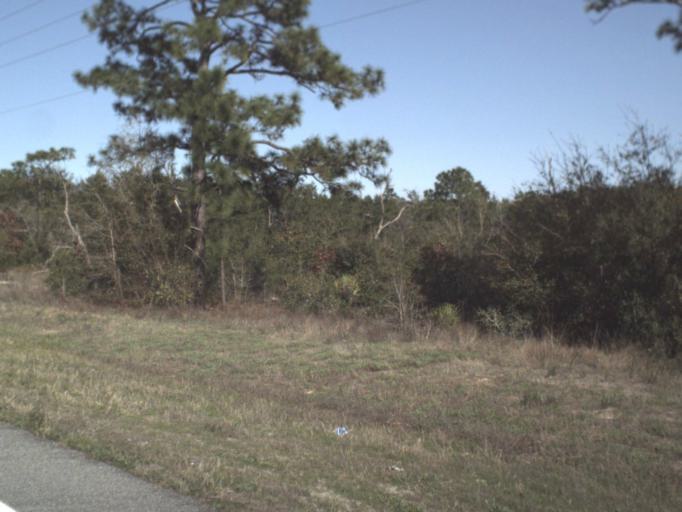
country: US
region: Florida
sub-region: Wakulla County
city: Crawfordville
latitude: 29.9318
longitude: -84.3961
